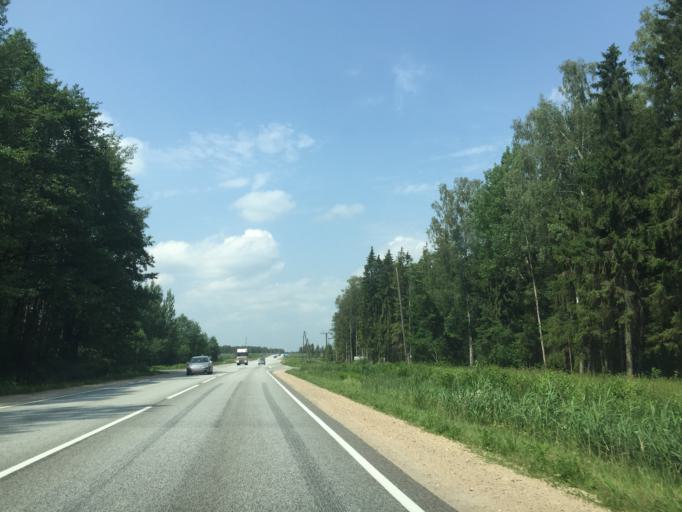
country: LV
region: Marupe
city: Marupe
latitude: 56.8303
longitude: 24.0490
